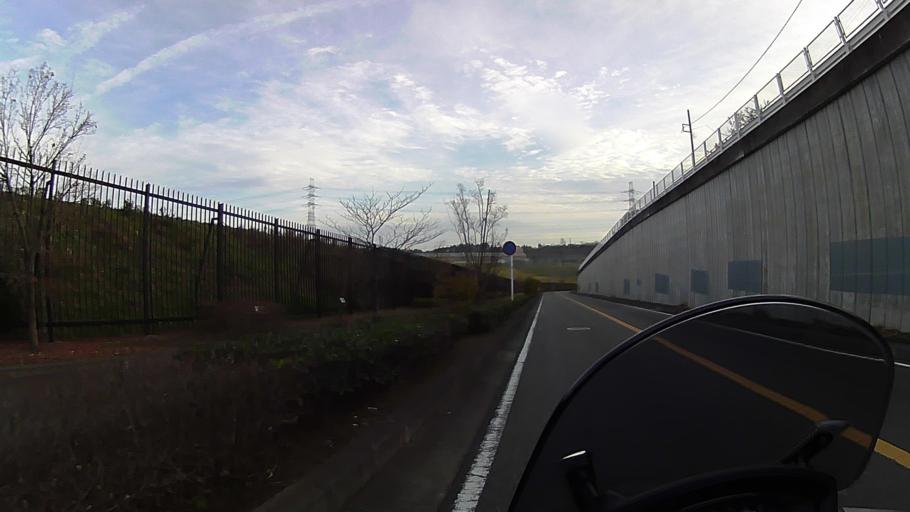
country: JP
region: Kanagawa
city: Atsugi
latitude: 35.4223
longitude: 139.4177
